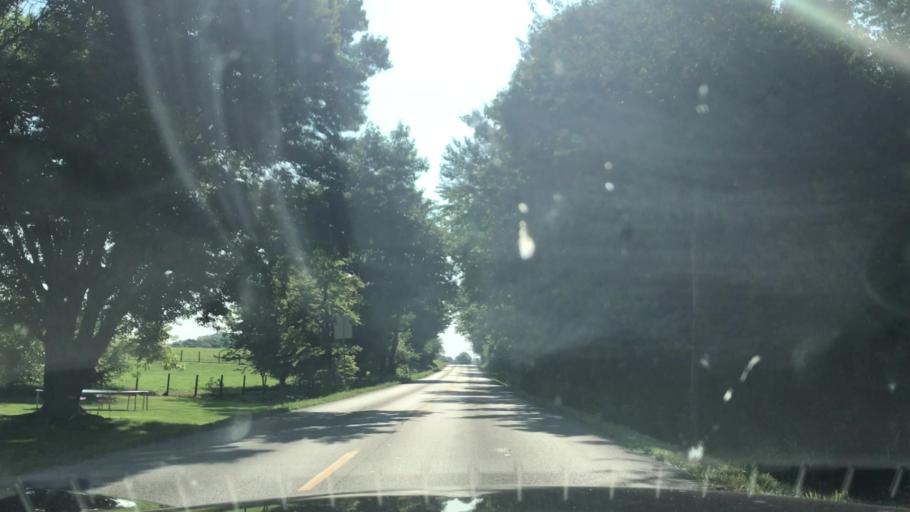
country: US
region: Kentucky
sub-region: Hart County
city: Horse Cave
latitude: 37.1665
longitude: -85.8375
